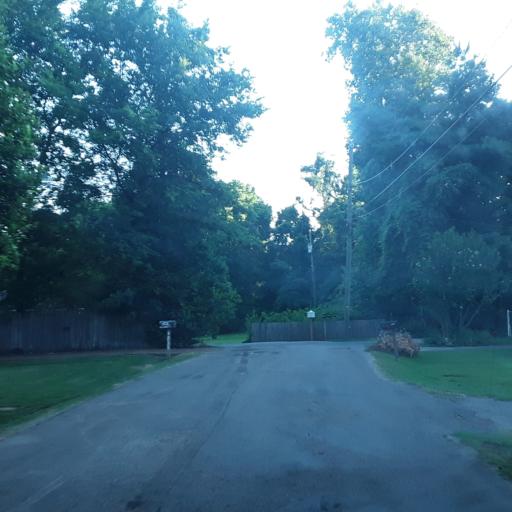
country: US
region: Tennessee
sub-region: Davidson County
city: Oak Hill
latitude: 36.1024
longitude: -86.7321
